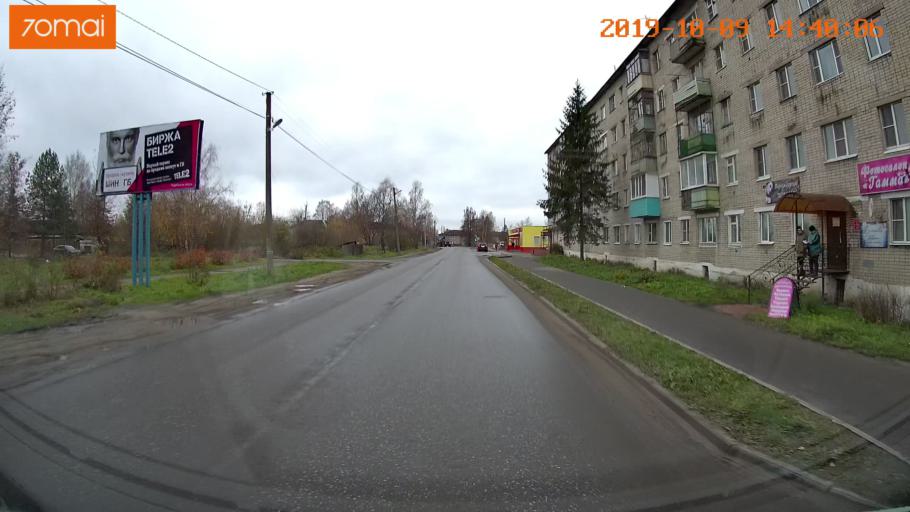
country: RU
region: Kostroma
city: Buy
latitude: 58.4760
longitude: 41.5357
